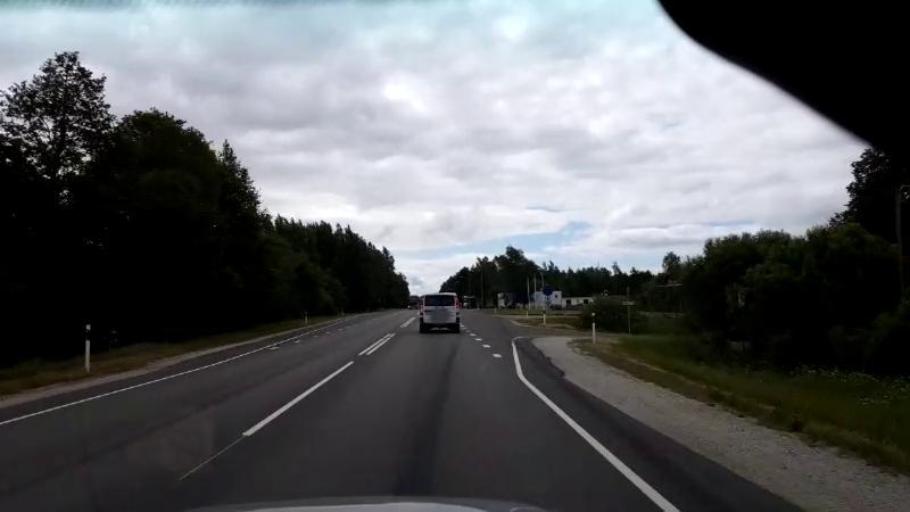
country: EE
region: Paernumaa
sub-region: Paernu linn
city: Parnu
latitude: 58.2048
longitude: 24.4854
